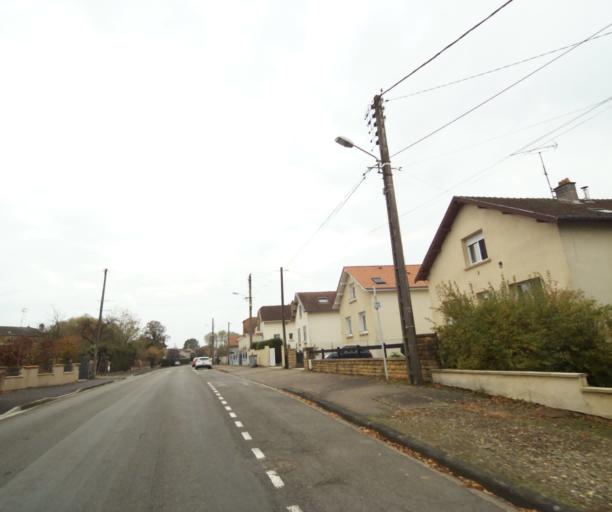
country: FR
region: Lorraine
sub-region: Departement de Meurthe-et-Moselle
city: Mancieulles
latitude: 49.2885
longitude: 5.8924
